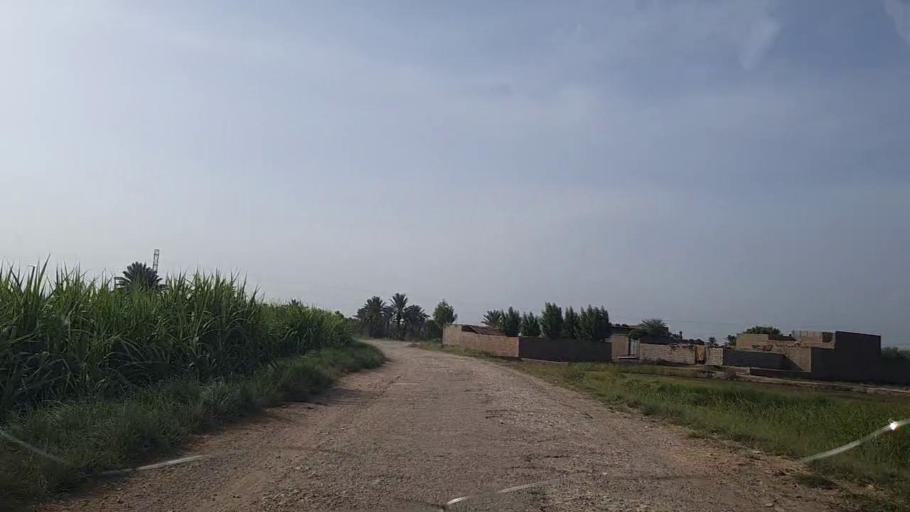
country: PK
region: Sindh
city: Ghotki
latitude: 28.0052
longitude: 69.2971
